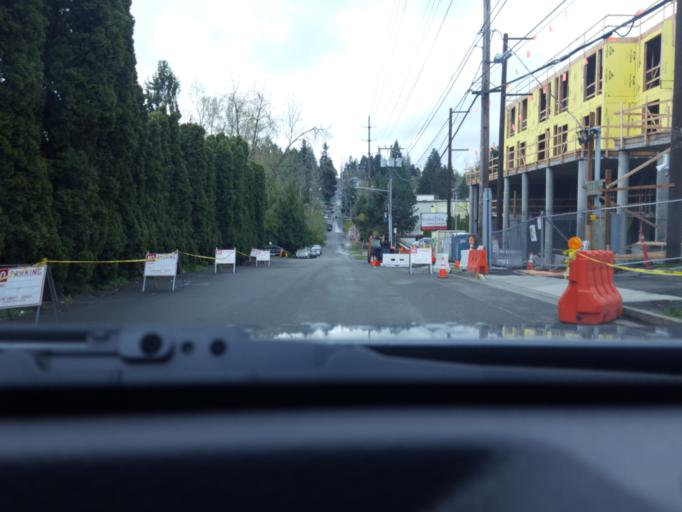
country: US
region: Washington
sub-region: King County
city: Shoreline
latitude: 47.7075
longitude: -122.3206
